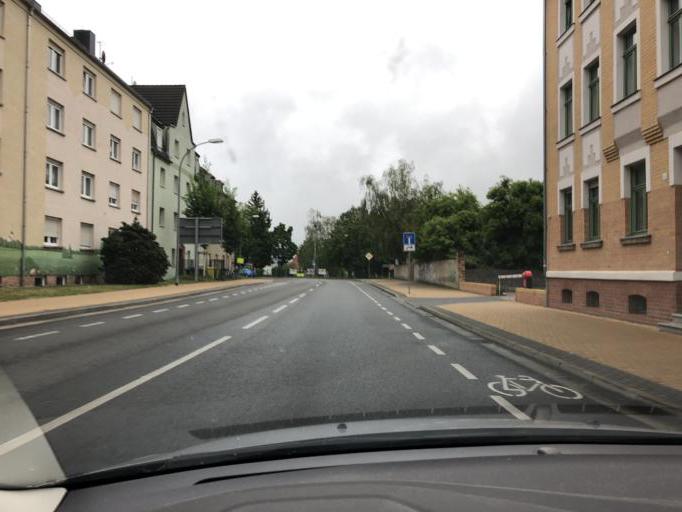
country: DE
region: Saxony
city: Delitzsch
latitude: 51.5307
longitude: 12.3364
